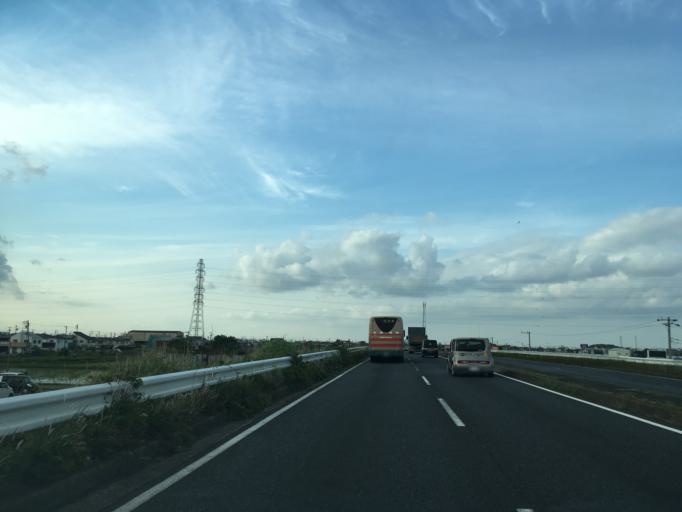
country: JP
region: Chiba
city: Kisarazu
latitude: 35.4005
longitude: 139.9416
